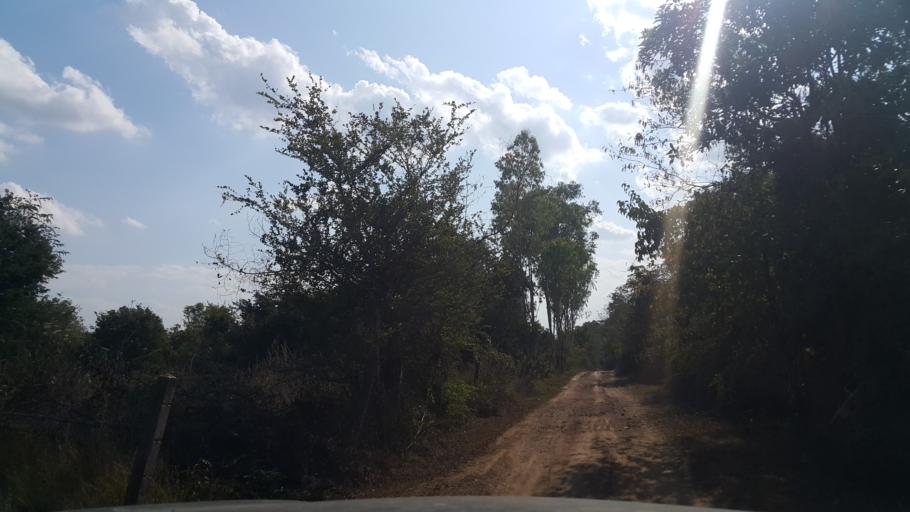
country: TH
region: Lamphun
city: Ban Thi
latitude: 18.5650
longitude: 99.1180
